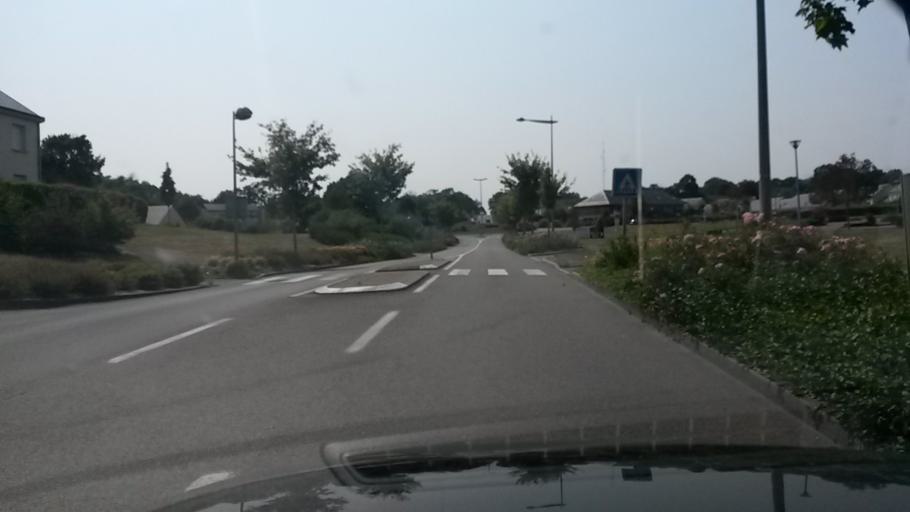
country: FR
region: Pays de la Loire
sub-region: Departement de la Mayenne
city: Saint-Fort
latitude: 47.8207
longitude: -0.7201
